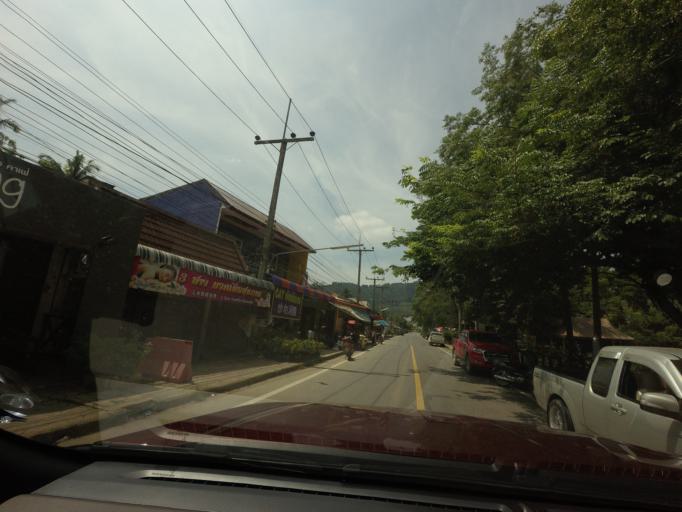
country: TH
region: Yala
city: Betong
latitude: 5.8501
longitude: 101.0723
